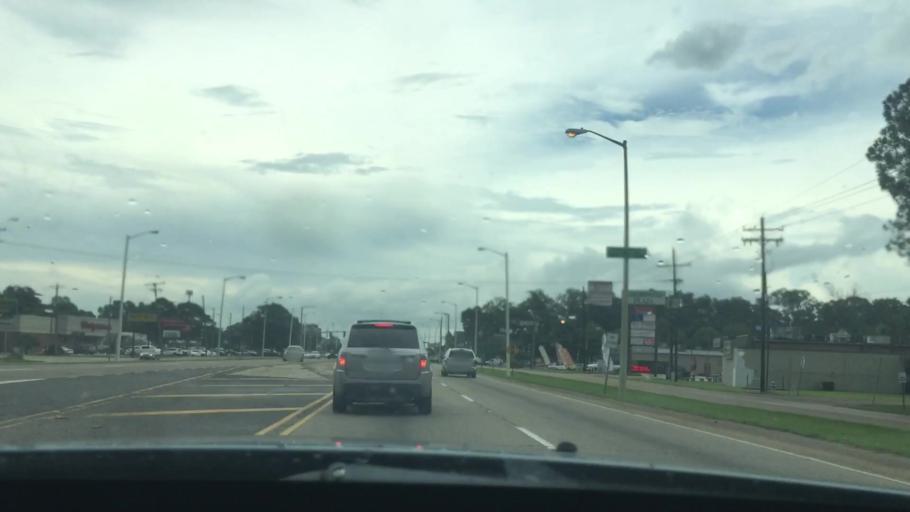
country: US
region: Louisiana
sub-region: East Baton Rouge Parish
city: Monticello
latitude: 30.4576
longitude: -91.0646
